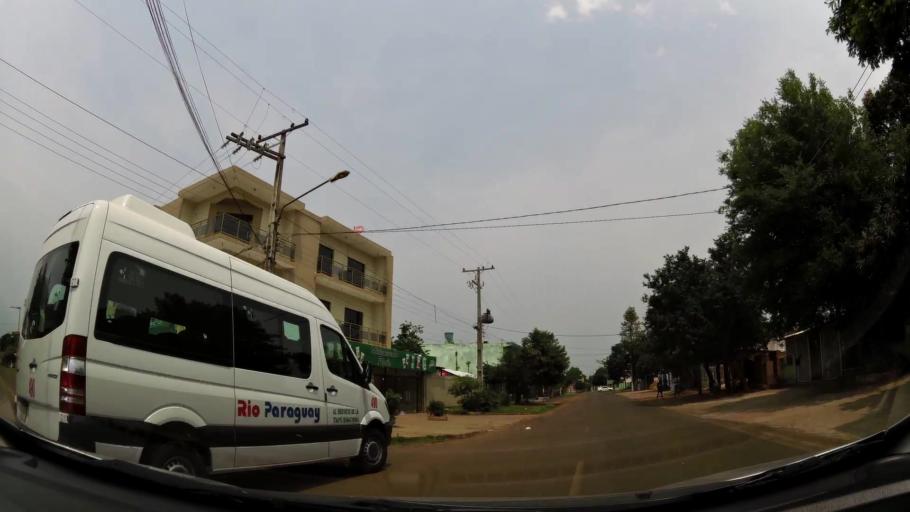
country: AR
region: Misiones
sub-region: Departamento de Iguazu
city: Puerto Iguazu
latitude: -25.5955
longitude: -54.6021
